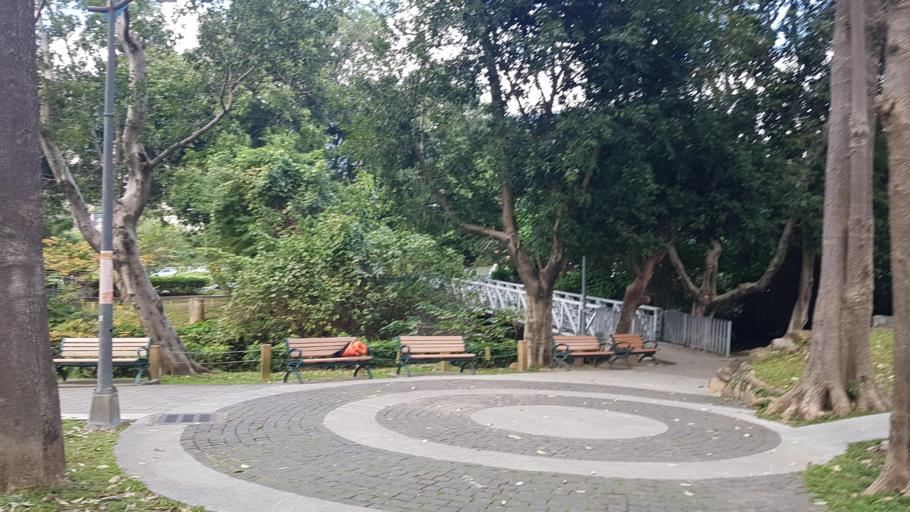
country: TW
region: Taipei
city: Taipei
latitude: 25.1397
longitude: 121.5037
